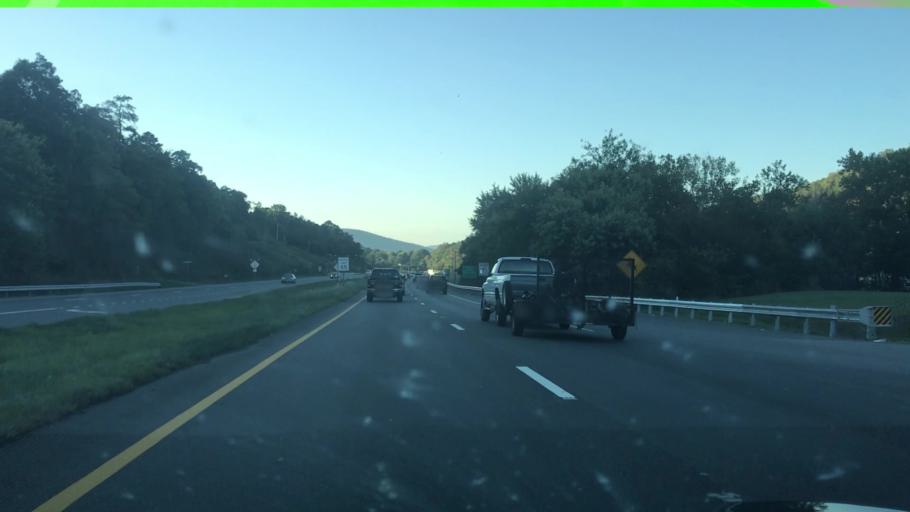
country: US
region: Virginia
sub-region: Botetourt County
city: Cloverdale
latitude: 37.3518
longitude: -79.8837
